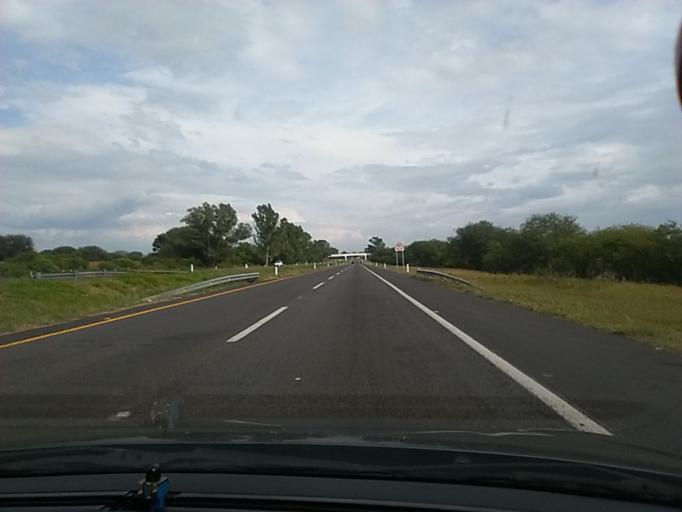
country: MX
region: Jalisco
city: La Barca
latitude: 20.3376
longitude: -102.6014
